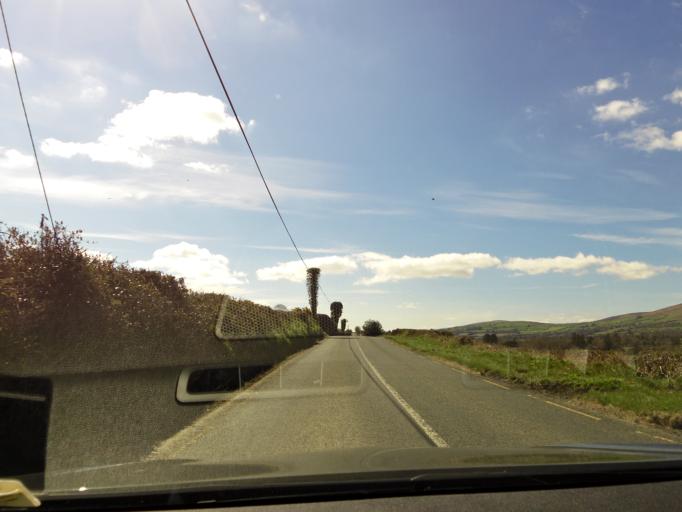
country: IE
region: Leinster
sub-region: Wicklow
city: Aughrim
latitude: 52.8194
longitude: -6.3861
